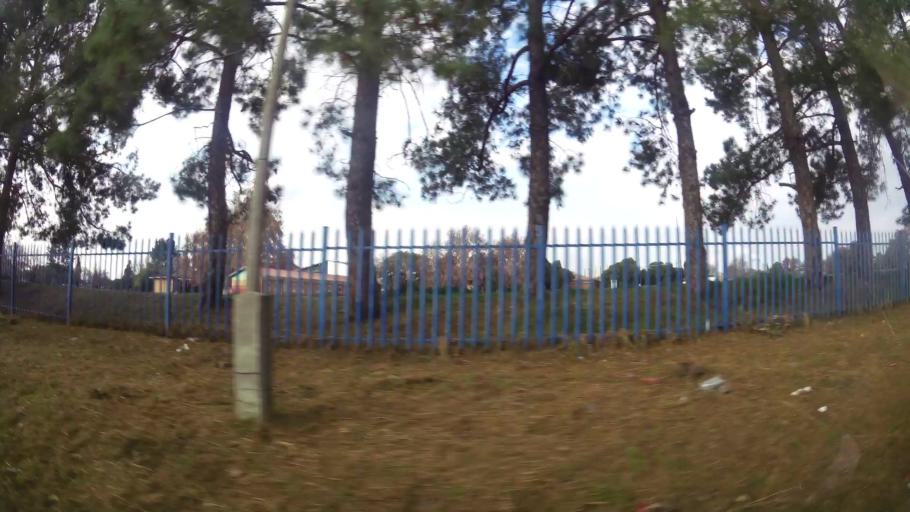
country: ZA
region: Orange Free State
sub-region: Fezile Dabi District Municipality
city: Sasolburg
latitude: -26.8231
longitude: 27.8279
